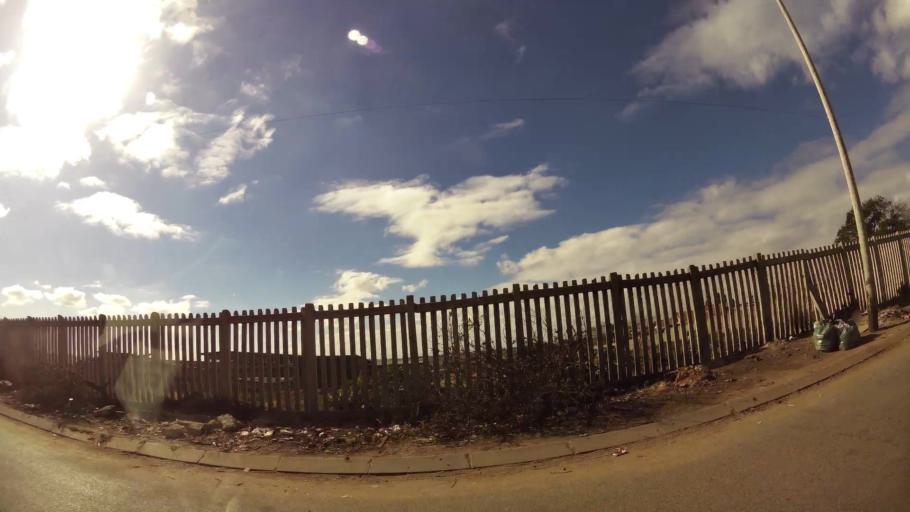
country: ZA
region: Gauteng
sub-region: City of Johannesburg Metropolitan Municipality
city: Modderfontein
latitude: -26.0463
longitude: 28.1800
